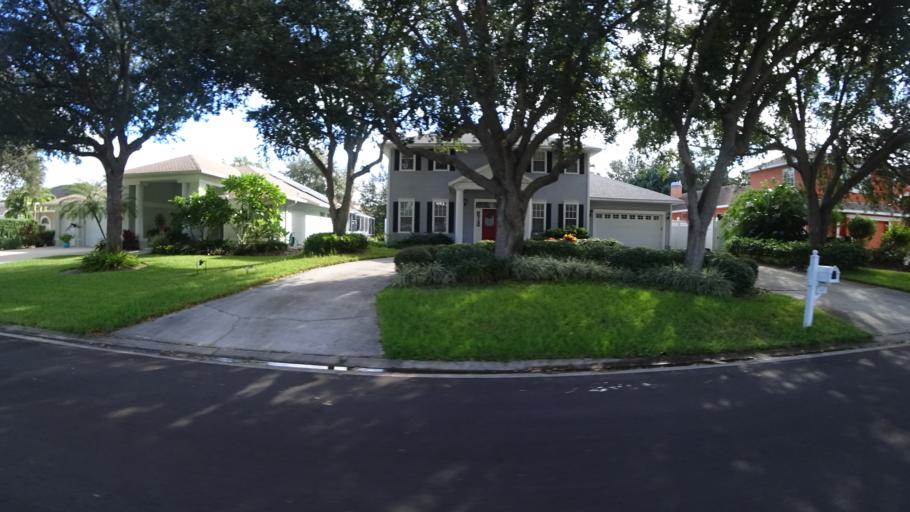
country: US
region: Florida
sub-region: Manatee County
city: West Bradenton
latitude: 27.5157
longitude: -82.6533
